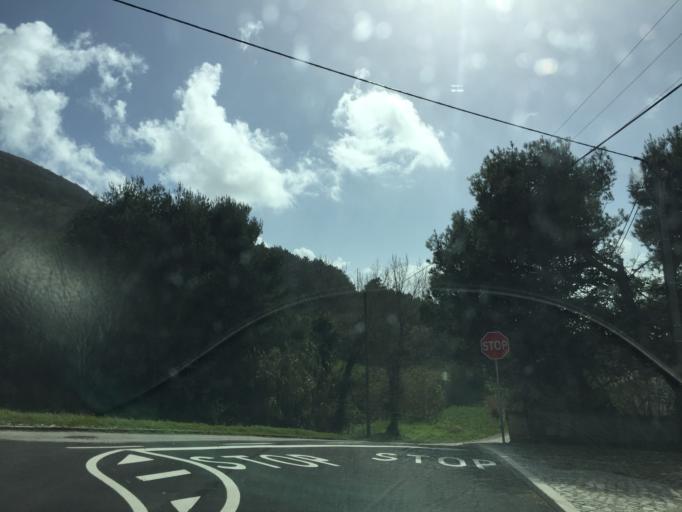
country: PT
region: Coimbra
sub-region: Figueira da Foz
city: Buarcos
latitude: 40.2070
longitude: -8.8933
